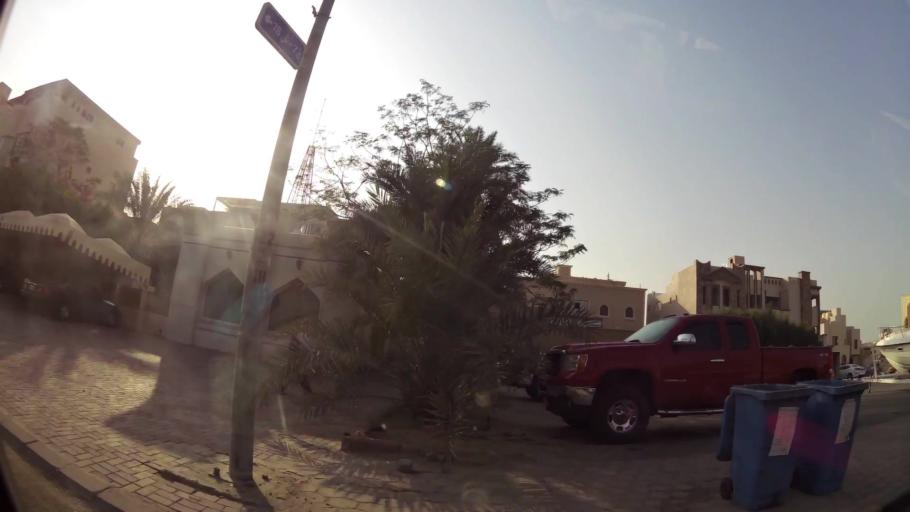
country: KW
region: Muhafazat Hawalli
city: Ar Rumaythiyah
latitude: 29.3212
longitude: 48.0771
